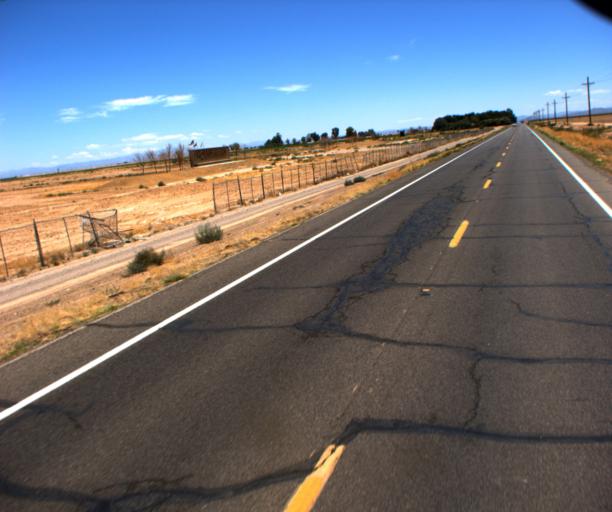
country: US
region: Arizona
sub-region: Pinal County
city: Casa Grande
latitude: 32.8798
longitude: -111.6359
